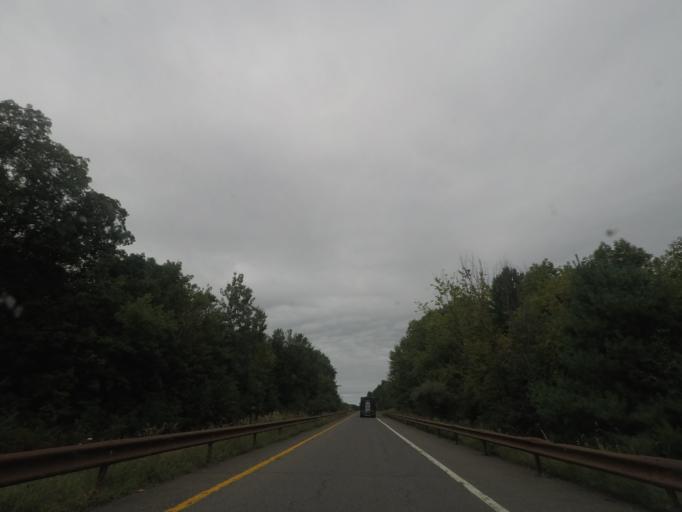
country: US
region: New York
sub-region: Columbia County
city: Chatham
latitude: 42.4075
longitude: -73.5480
